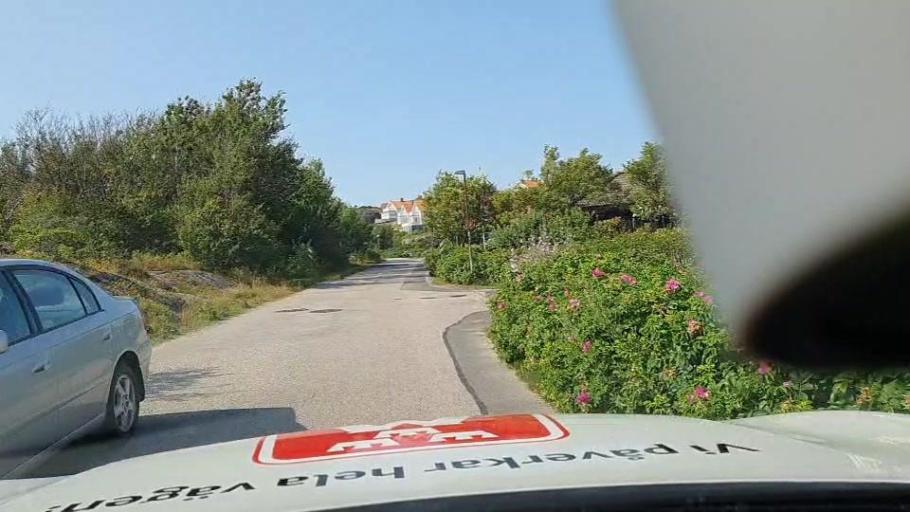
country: SE
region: Vaestra Goetaland
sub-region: Lysekils Kommun
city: Lysekil
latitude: 58.1200
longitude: 11.4487
